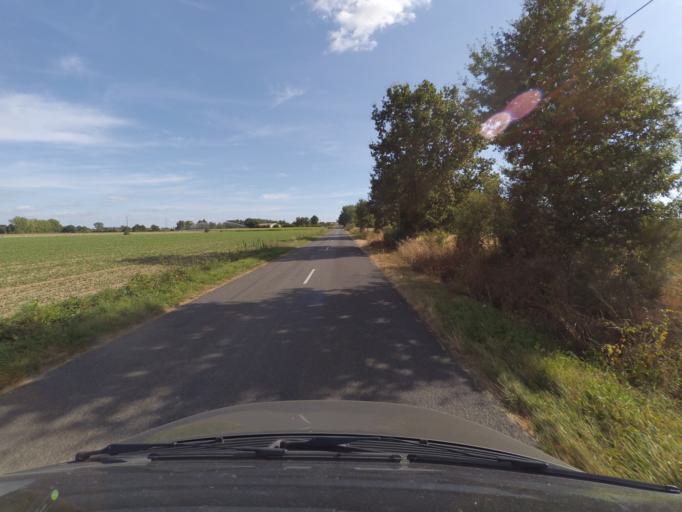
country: FR
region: Pays de la Loire
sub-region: Departement de la Loire-Atlantique
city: La Planche
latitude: 47.0025
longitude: -1.4551
